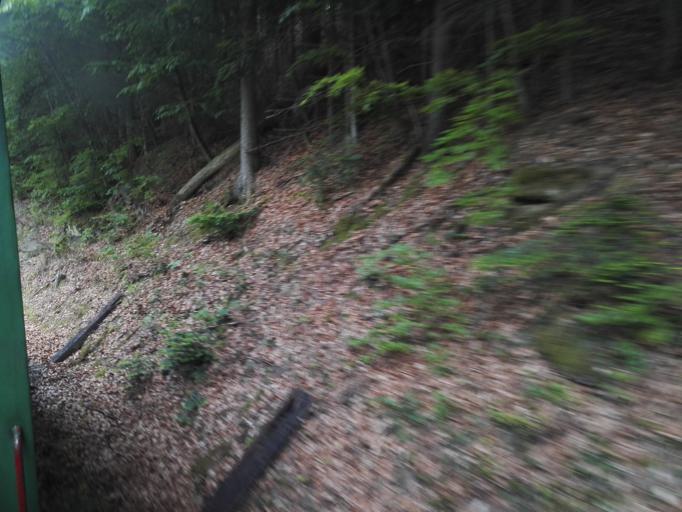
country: AT
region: Styria
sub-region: Politischer Bezirk Weiz
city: Anger
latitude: 47.2918
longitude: 15.6930
